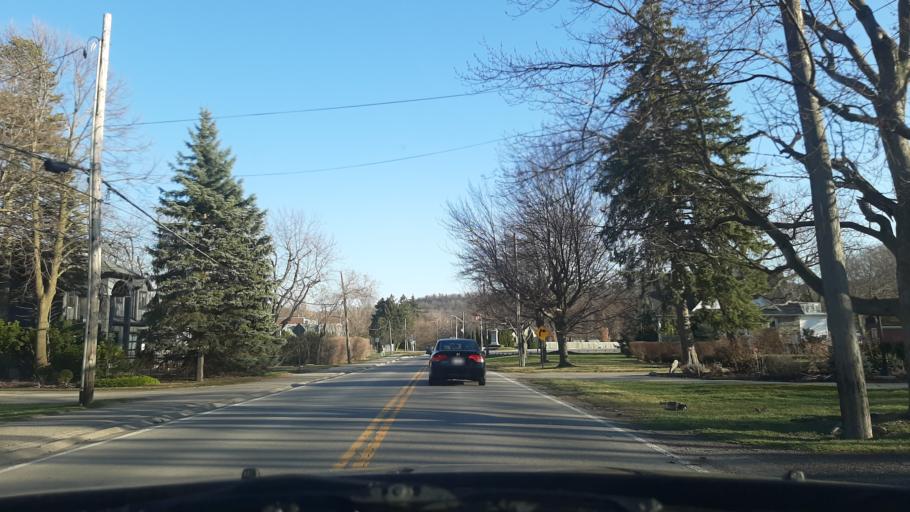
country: US
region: New York
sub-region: Niagara County
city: Lewiston
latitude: 43.1714
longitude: -79.0584
